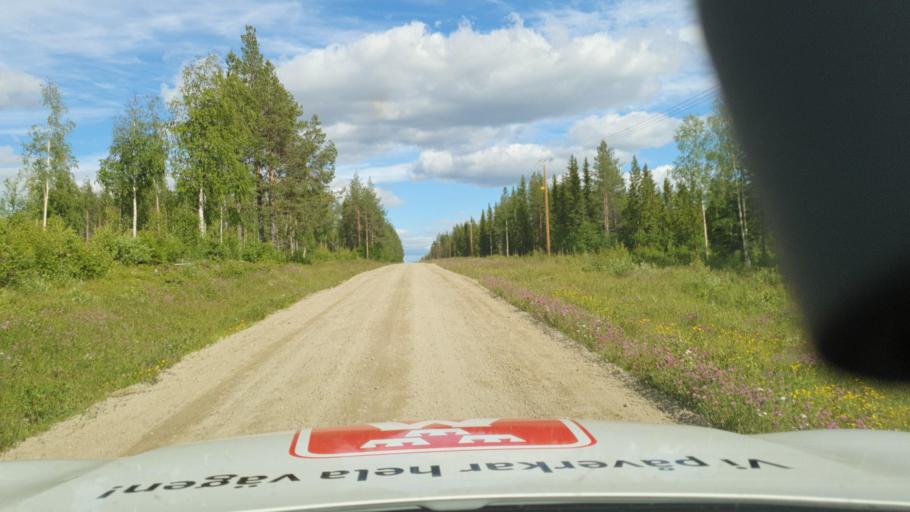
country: SE
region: Vaesterbotten
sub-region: Lycksele Kommun
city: Lycksele
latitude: 64.2965
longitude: 18.2392
